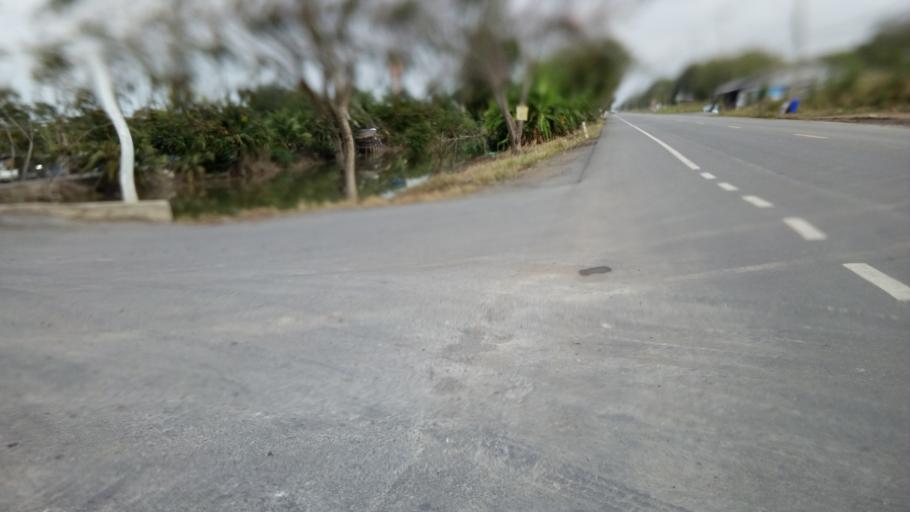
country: TH
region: Pathum Thani
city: Nong Suea
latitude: 14.1687
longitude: 100.8236
